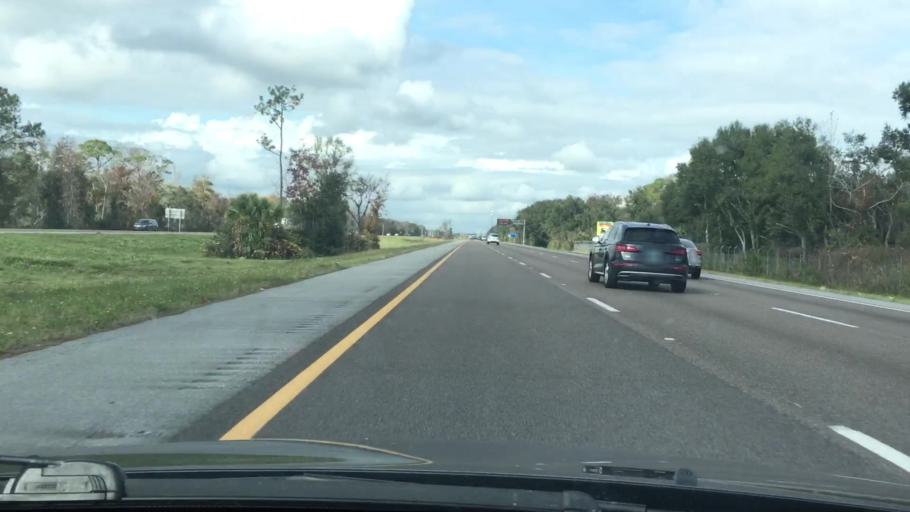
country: US
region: Florida
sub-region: Volusia County
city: Edgewater
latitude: 28.9351
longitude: -80.9432
